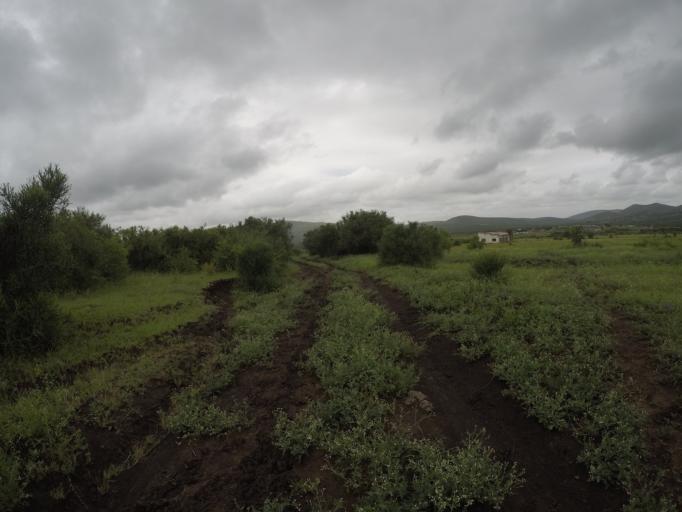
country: ZA
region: KwaZulu-Natal
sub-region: uThungulu District Municipality
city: Empangeni
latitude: -28.6020
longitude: 31.8615
